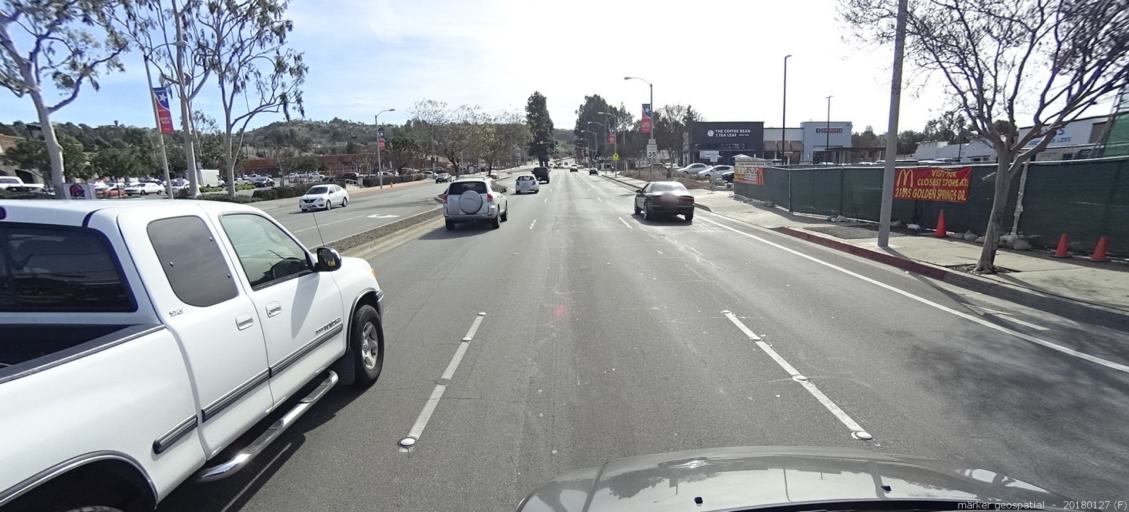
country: US
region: California
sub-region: Los Angeles County
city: Diamond Bar
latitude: 34.0219
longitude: -117.8108
